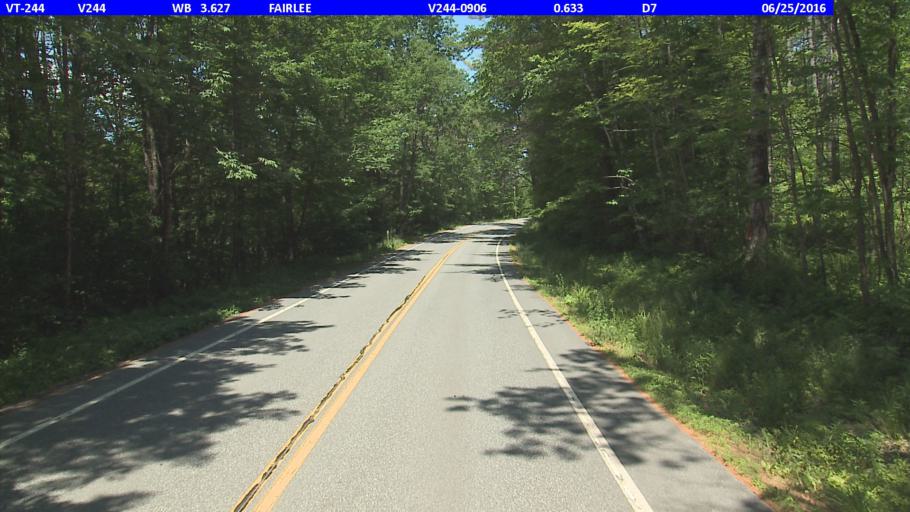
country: US
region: New Hampshire
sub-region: Grafton County
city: Orford
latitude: 43.8958
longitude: -72.2077
